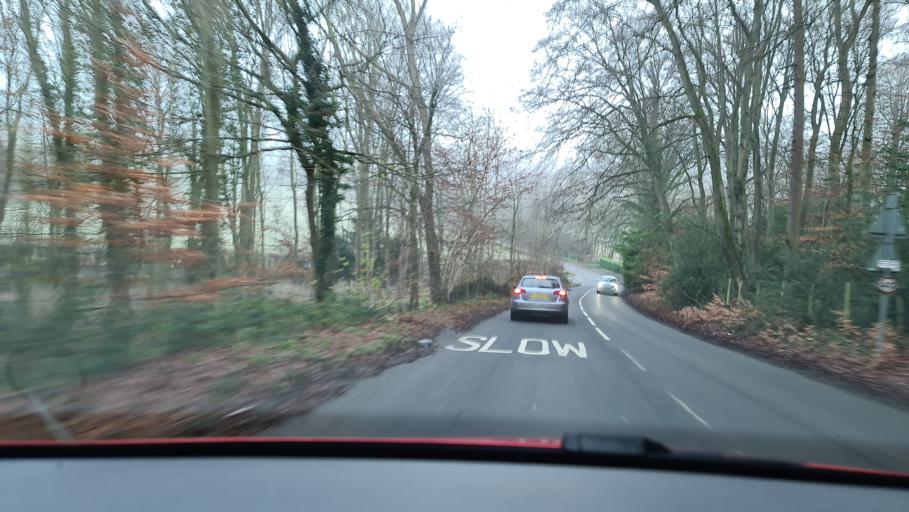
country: GB
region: England
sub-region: Buckinghamshire
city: Seer Green
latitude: 51.6074
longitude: -0.5970
